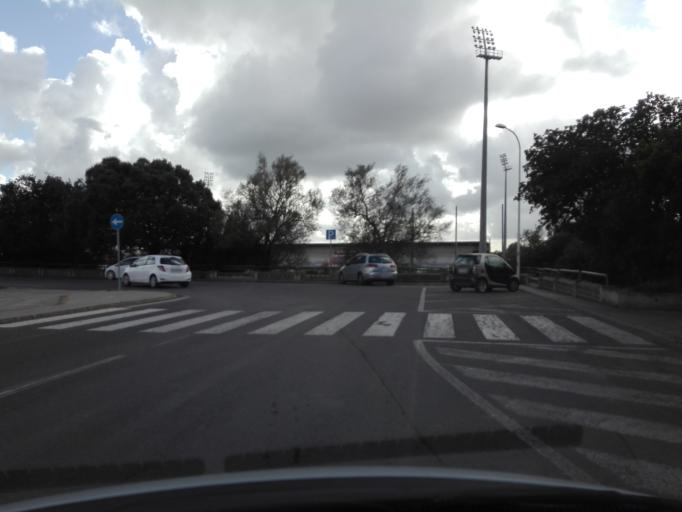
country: IT
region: Sardinia
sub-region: Provincia di Sassari
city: Sassari
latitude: 40.7188
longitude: 8.5819
